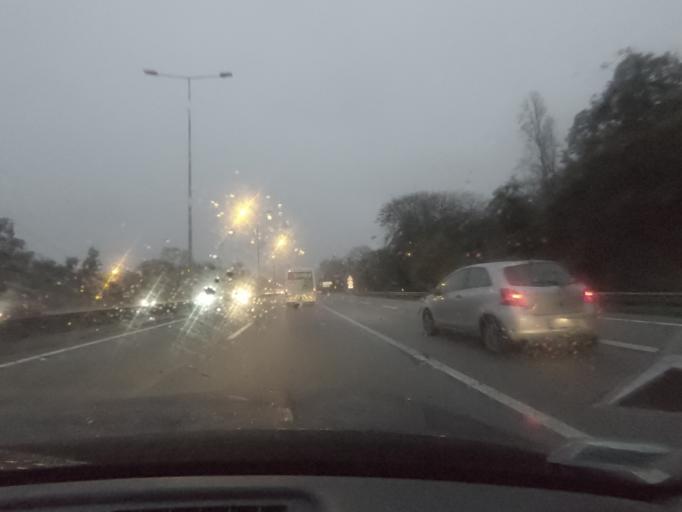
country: PT
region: Porto
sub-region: Matosinhos
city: Leca da Palmeira
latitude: 41.1984
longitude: -8.6862
